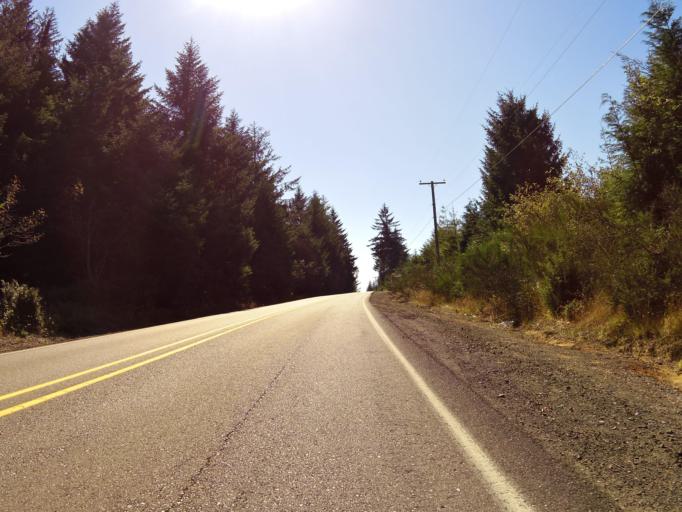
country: US
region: Oregon
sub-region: Coos County
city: Barview
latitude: 43.3241
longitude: -124.3414
